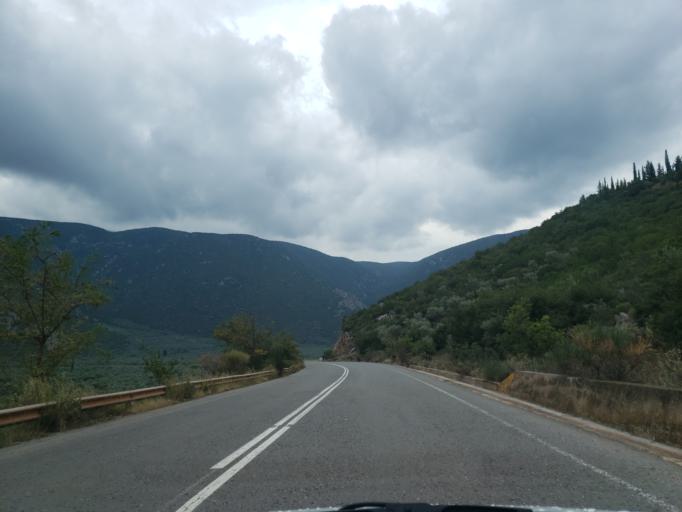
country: GR
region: Central Greece
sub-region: Nomos Fokidos
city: Amfissa
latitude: 38.5418
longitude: 22.4114
